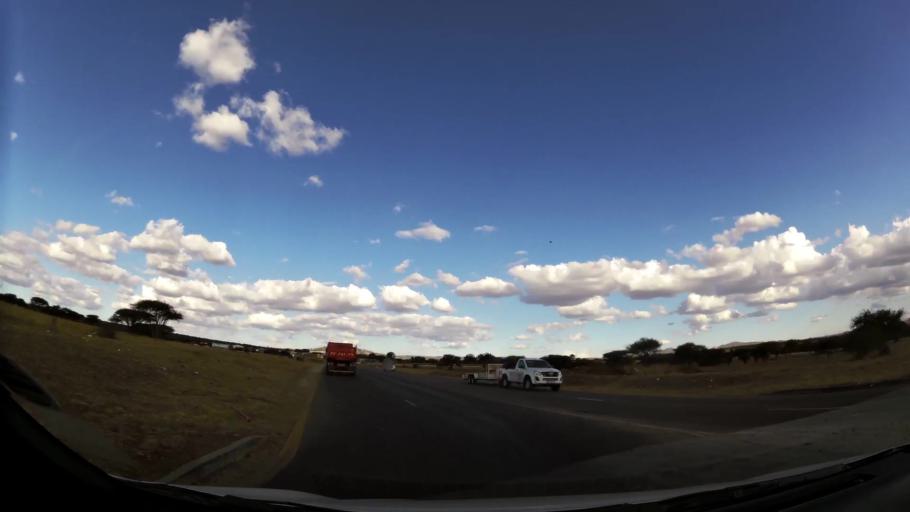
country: ZA
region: Limpopo
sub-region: Capricorn District Municipality
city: Polokwane
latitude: -23.9273
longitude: 29.4685
